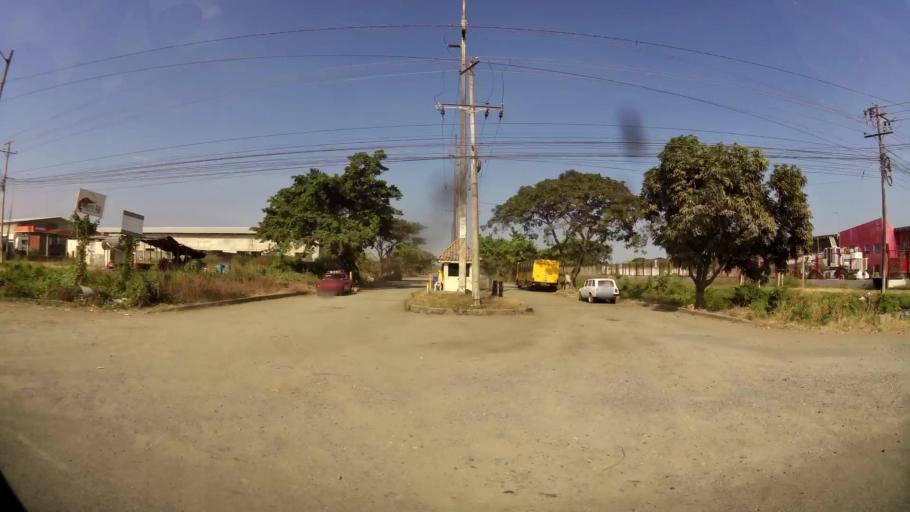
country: EC
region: Guayas
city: Eloy Alfaro
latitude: -2.1952
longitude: -79.8213
